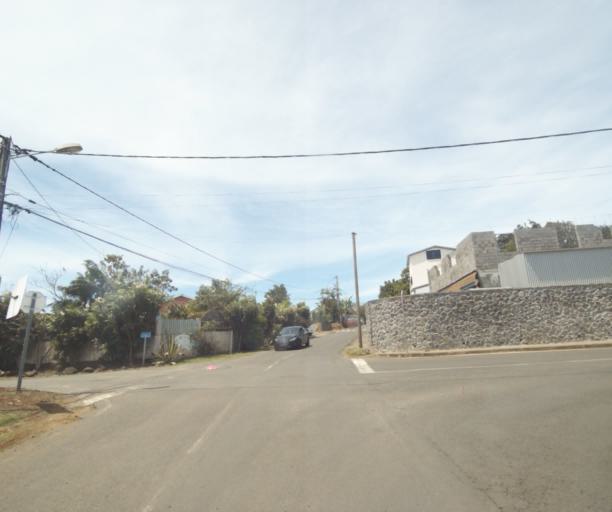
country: RE
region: Reunion
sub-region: Reunion
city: Saint-Paul
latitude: -21.0445
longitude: 55.2808
